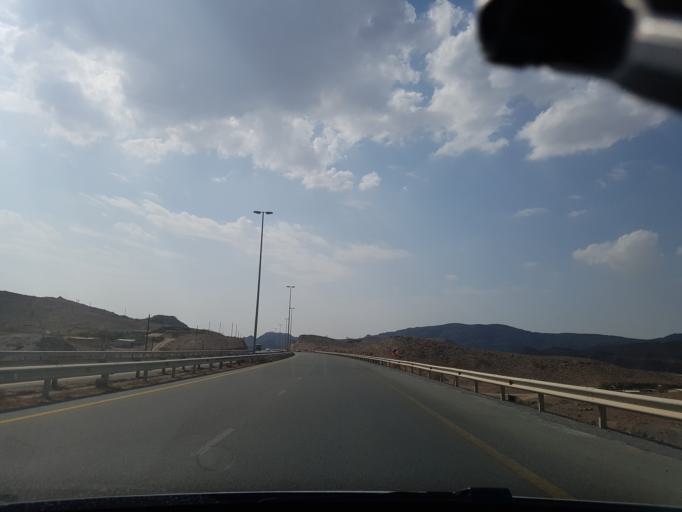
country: AE
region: Al Fujayrah
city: Dibba Al-Fujairah
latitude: 25.5166
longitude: 56.0880
